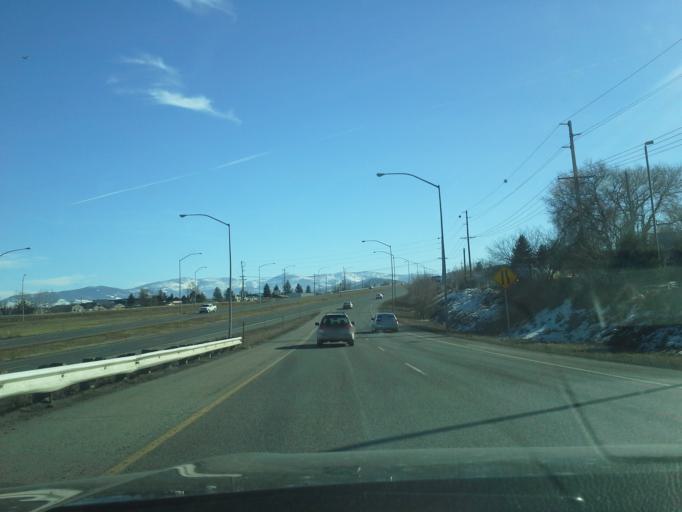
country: US
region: Montana
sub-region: Lewis and Clark County
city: Helena
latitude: 46.6059
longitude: -112.0081
